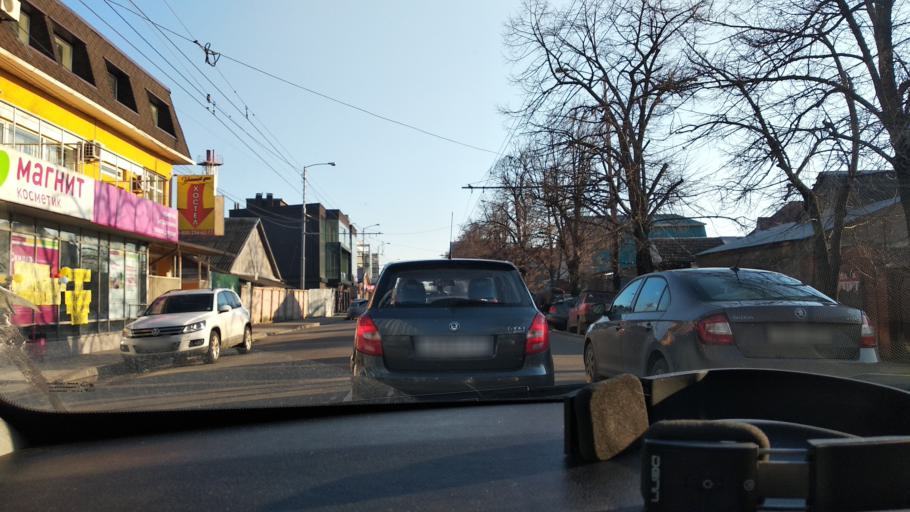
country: RU
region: Adygeya
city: Yablonovskiy
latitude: 45.0033
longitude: 38.9610
